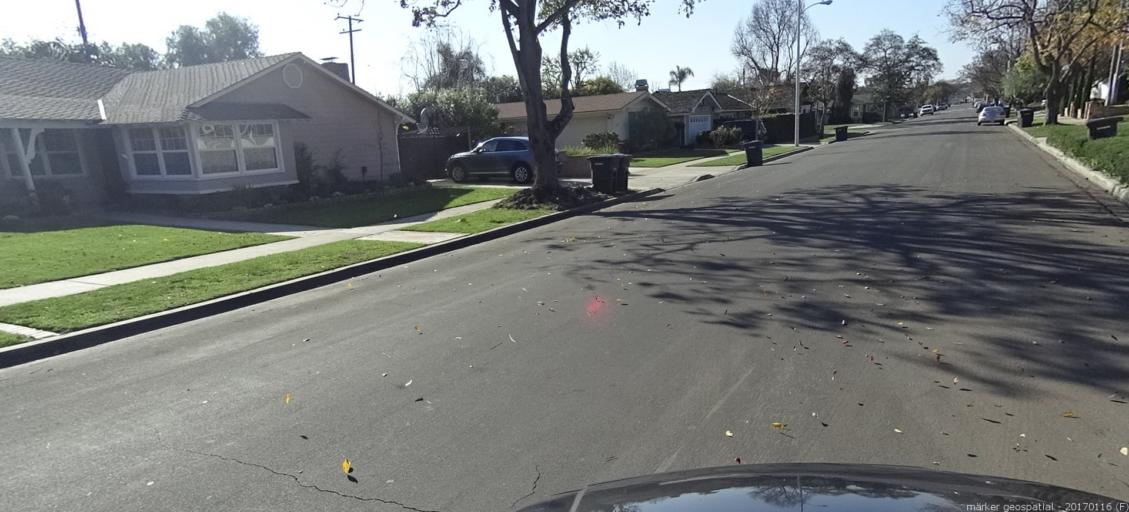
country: US
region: California
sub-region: Orange County
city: Rossmoor
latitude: 33.7832
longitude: -118.0828
